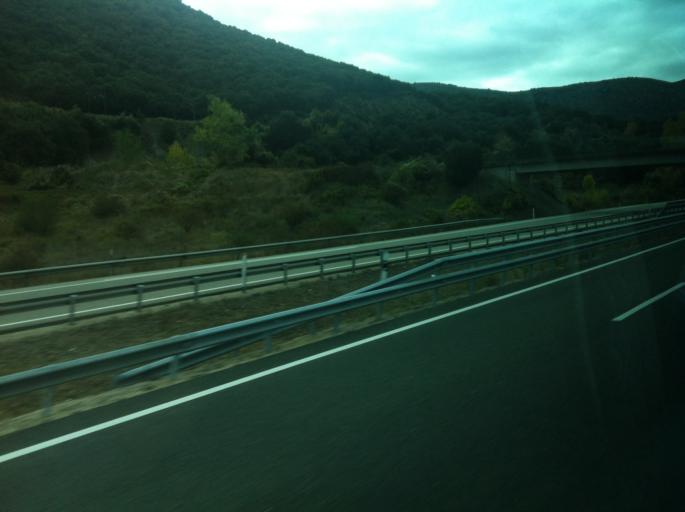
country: ES
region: Castille and Leon
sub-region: Provincia de Burgos
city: Ameyugo
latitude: 42.6538
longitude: -3.0619
